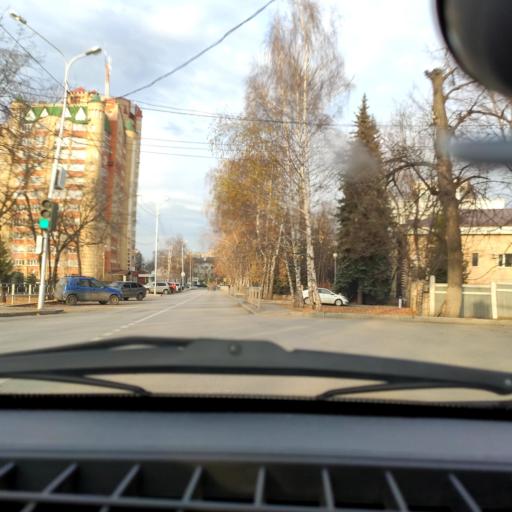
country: RU
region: Bashkortostan
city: Ufa
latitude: 54.7206
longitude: 56.0139
